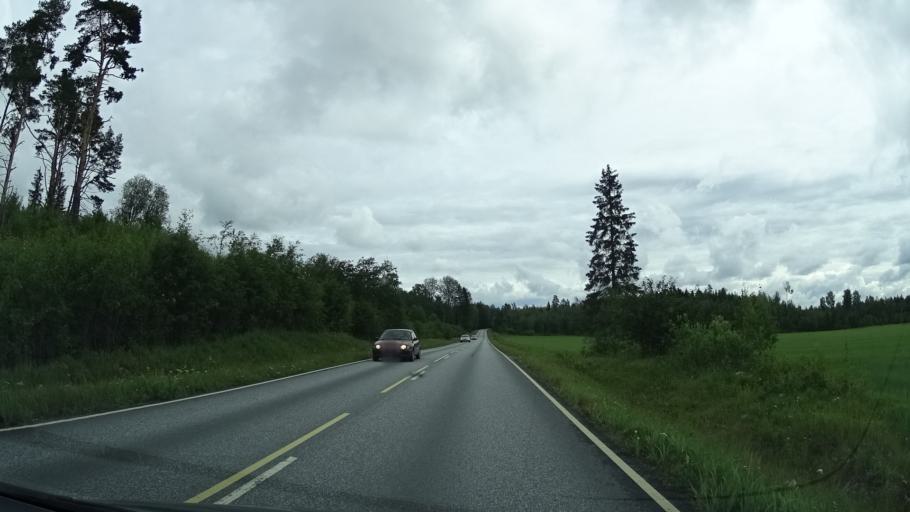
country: FI
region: Pirkanmaa
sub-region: Etelae-Pirkanmaa
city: Urjala
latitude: 61.0925
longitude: 23.3851
